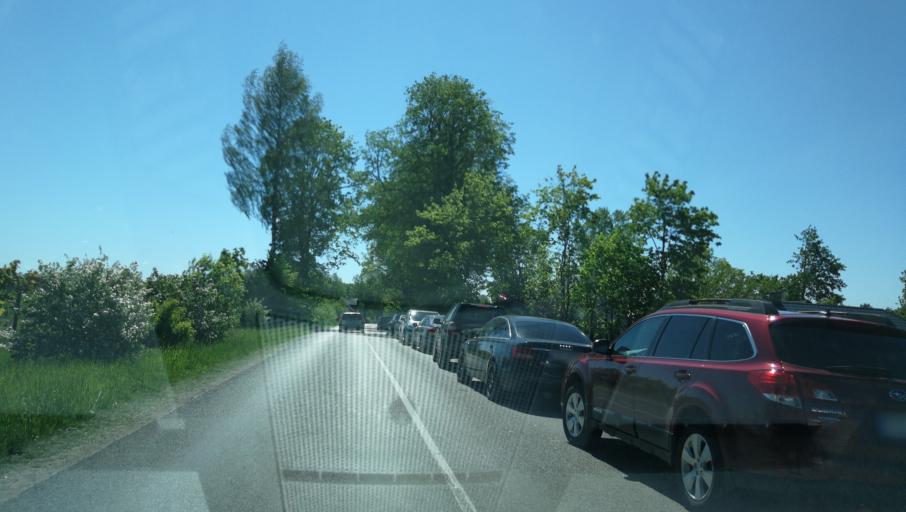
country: LV
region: Dobeles Rajons
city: Dobele
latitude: 56.6067
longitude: 23.2994
